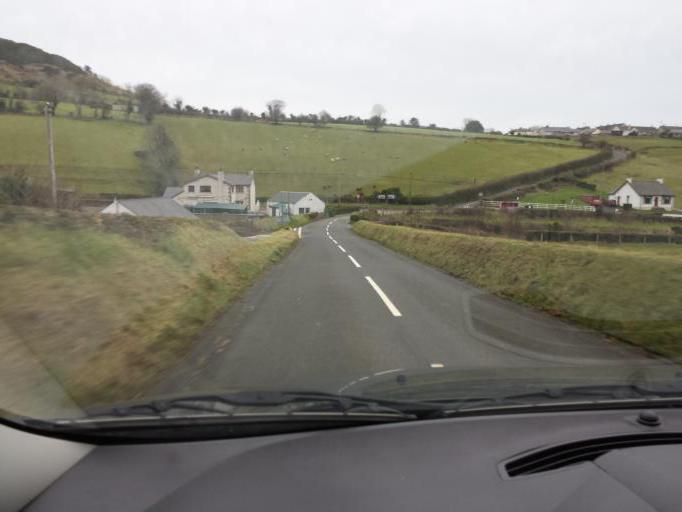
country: GB
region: Northern Ireland
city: Cushendall
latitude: 55.0836
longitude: -6.0778
